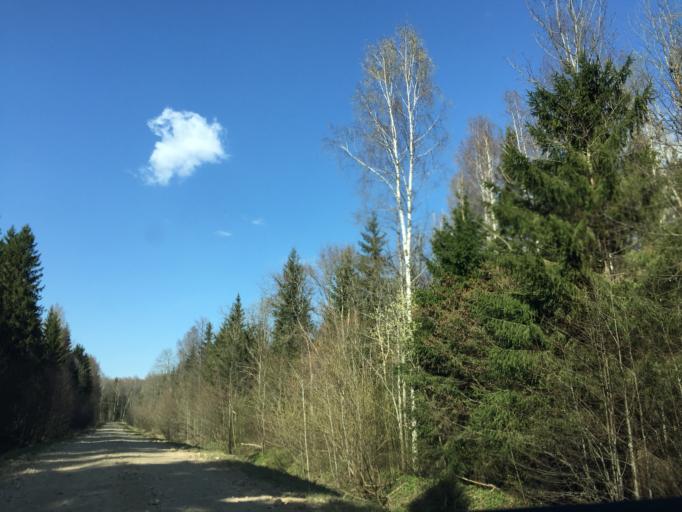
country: LV
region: Lielvarde
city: Lielvarde
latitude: 56.8513
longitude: 24.8036
